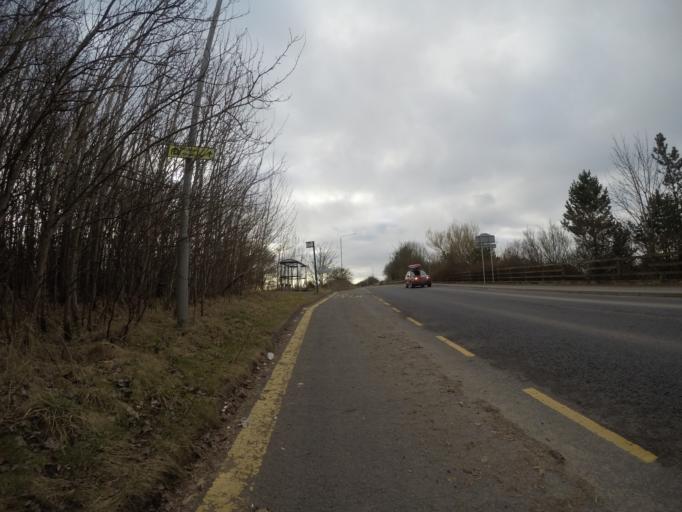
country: GB
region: Scotland
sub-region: South Ayrshire
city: Troon
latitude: 55.5699
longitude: -4.6392
